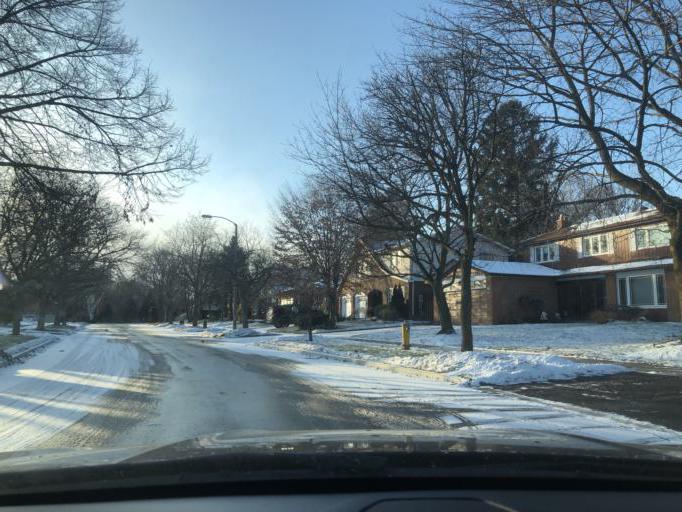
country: CA
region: Ontario
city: Scarborough
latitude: 43.7797
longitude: -79.1496
